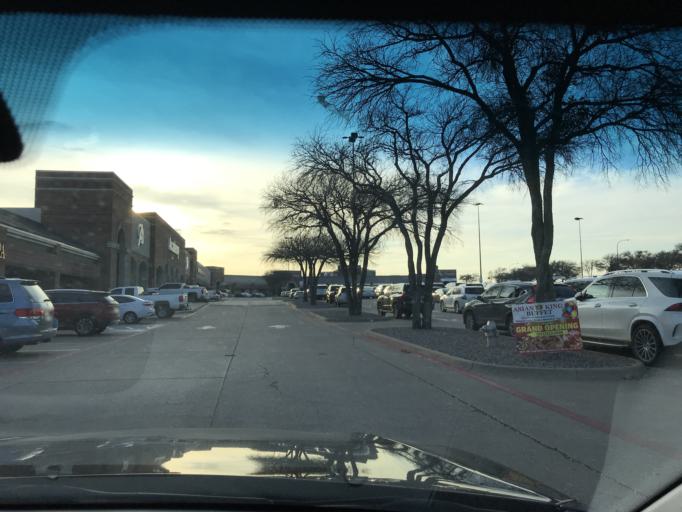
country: US
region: Texas
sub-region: Tarrant County
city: Benbrook
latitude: 32.6818
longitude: -97.4156
